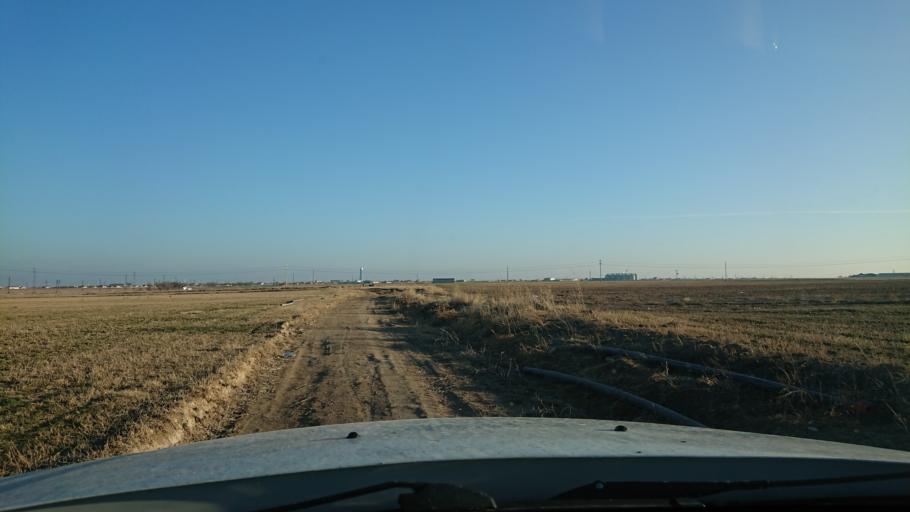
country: TR
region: Aksaray
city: Sultanhani
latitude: 38.2673
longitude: 33.5205
